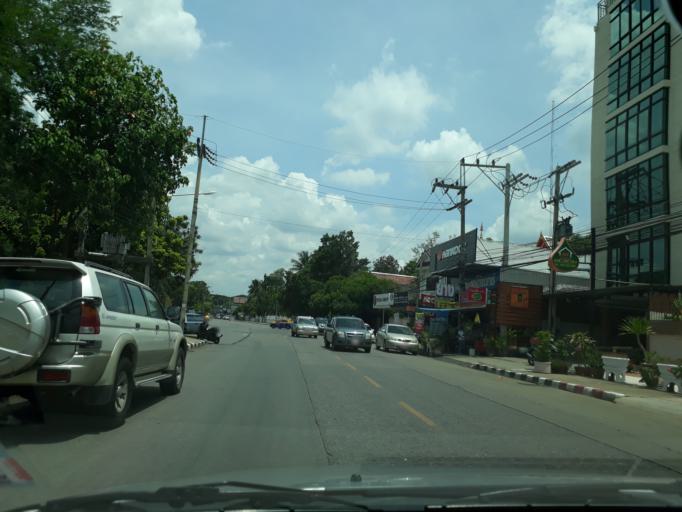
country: TH
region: Khon Kaen
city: Khon Kaen
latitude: 16.4109
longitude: 102.8351
